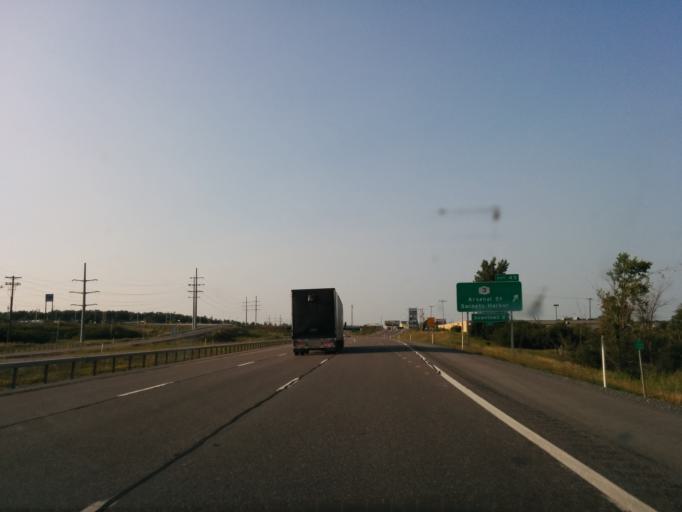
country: US
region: New York
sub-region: Jefferson County
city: Watertown
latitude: 43.9712
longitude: -75.9484
